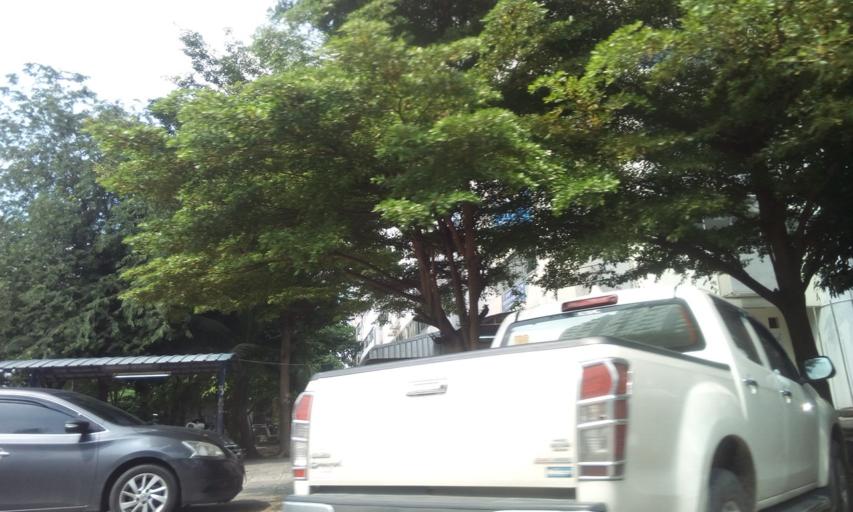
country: TH
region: Bangkok
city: Don Mueang
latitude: 13.9185
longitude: 100.5537
